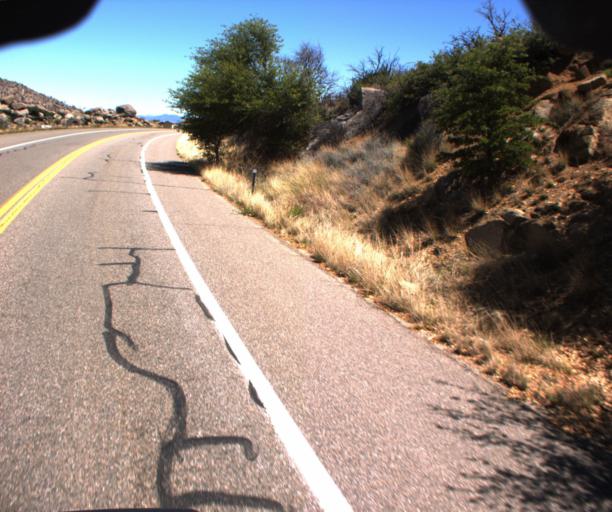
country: US
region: Arizona
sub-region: Yavapai County
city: Congress
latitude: 34.2143
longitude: -112.7553
